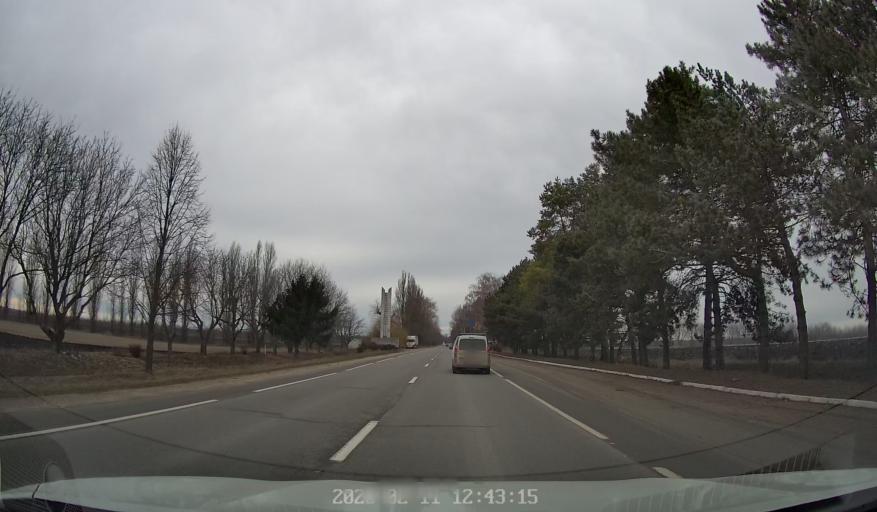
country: MD
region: Raionul Edinet
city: Edinet
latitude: 48.2310
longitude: 27.2124
